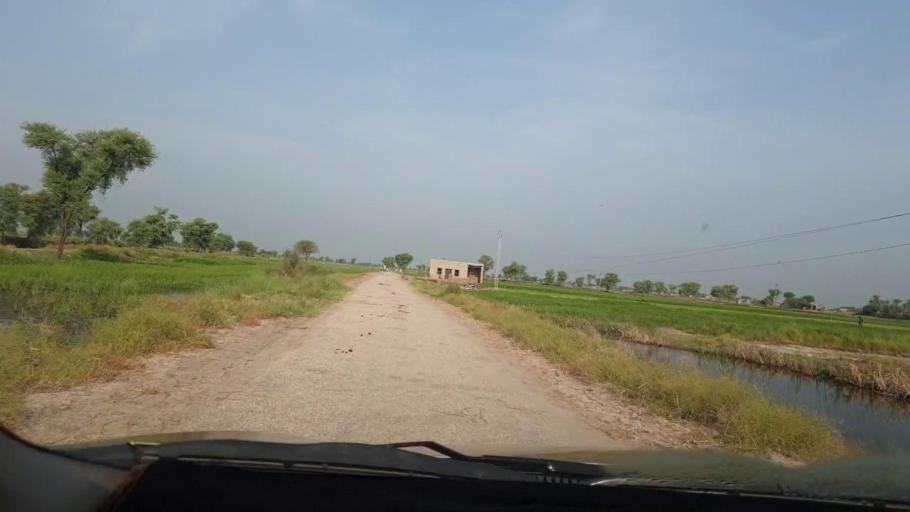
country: PK
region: Sindh
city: Goth Garelo
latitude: 27.4838
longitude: 68.0681
